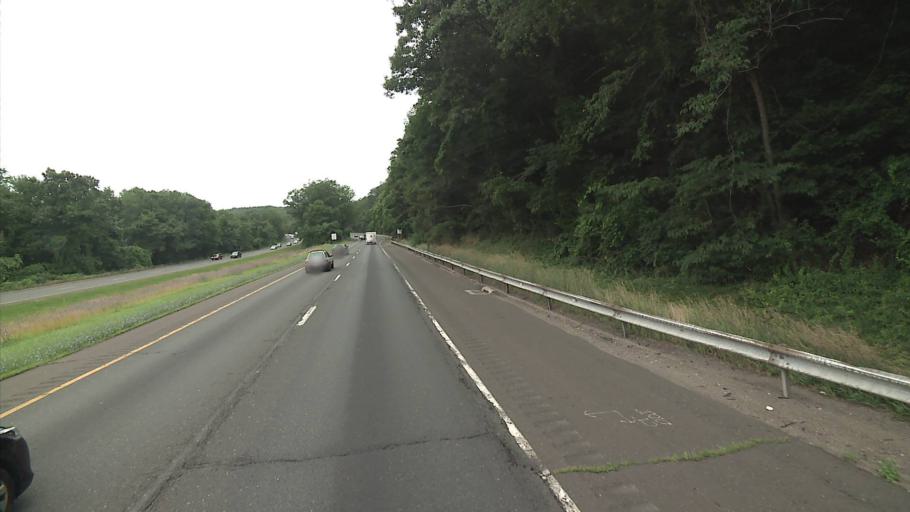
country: US
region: Connecticut
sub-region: Fairfield County
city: Newtown
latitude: 41.4278
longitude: -73.3095
